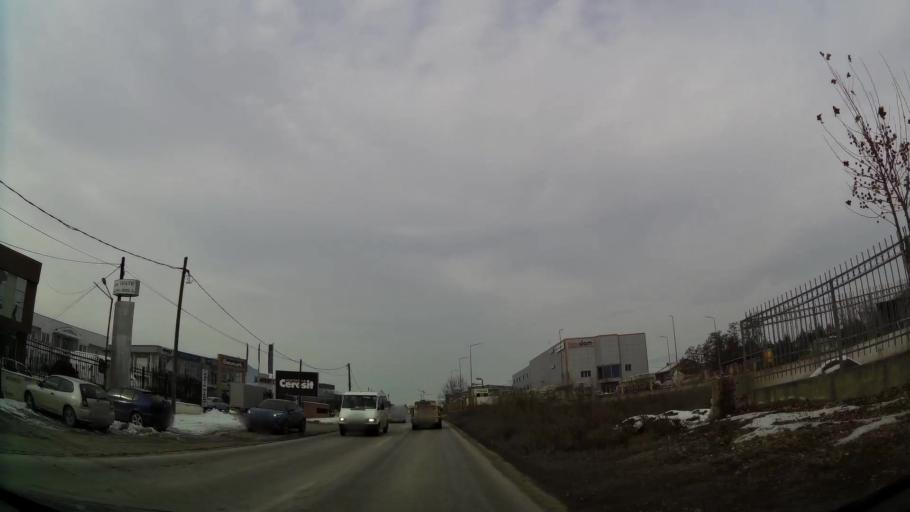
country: MK
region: Suto Orizari
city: Suto Orizare
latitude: 42.0407
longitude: 21.3944
